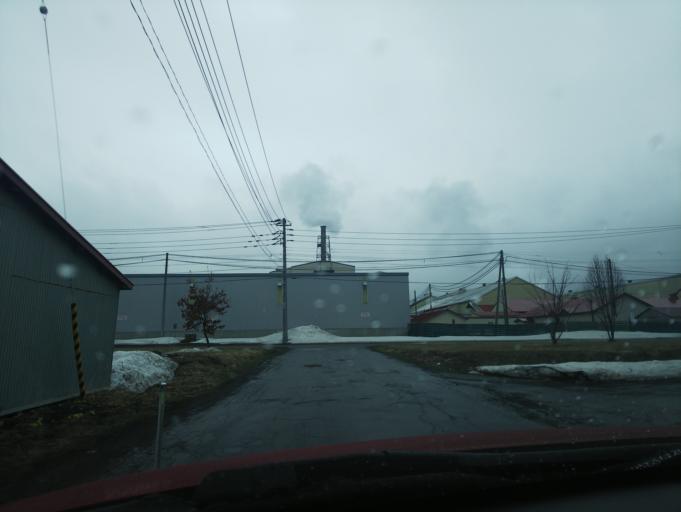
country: JP
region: Hokkaido
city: Nayoro
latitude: 44.3417
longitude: 142.4604
